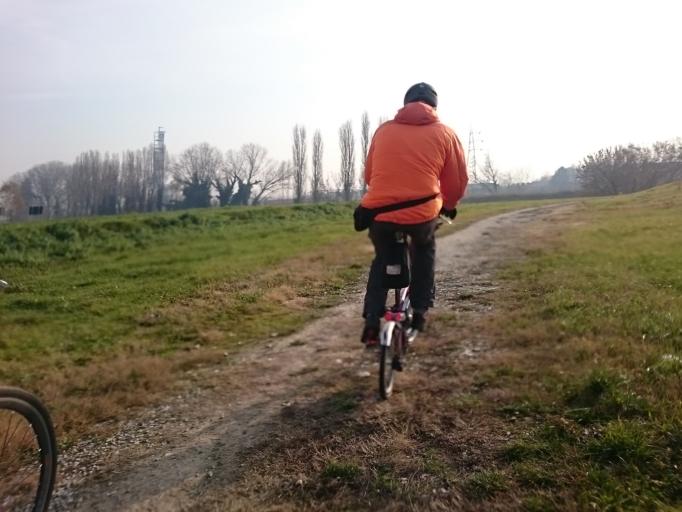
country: IT
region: Veneto
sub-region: Provincia di Padova
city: Noventa
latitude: 45.4063
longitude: 11.9223
